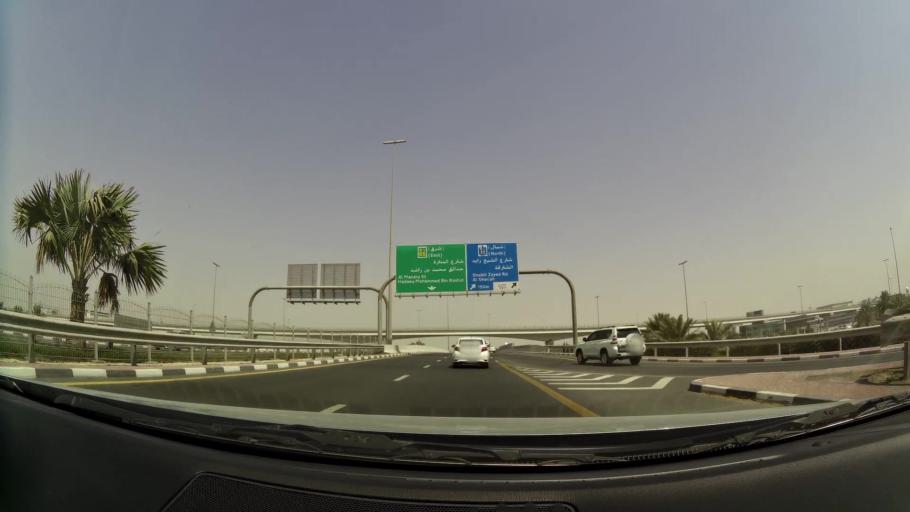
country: AE
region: Dubai
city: Dubai
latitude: 25.1498
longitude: 55.2231
